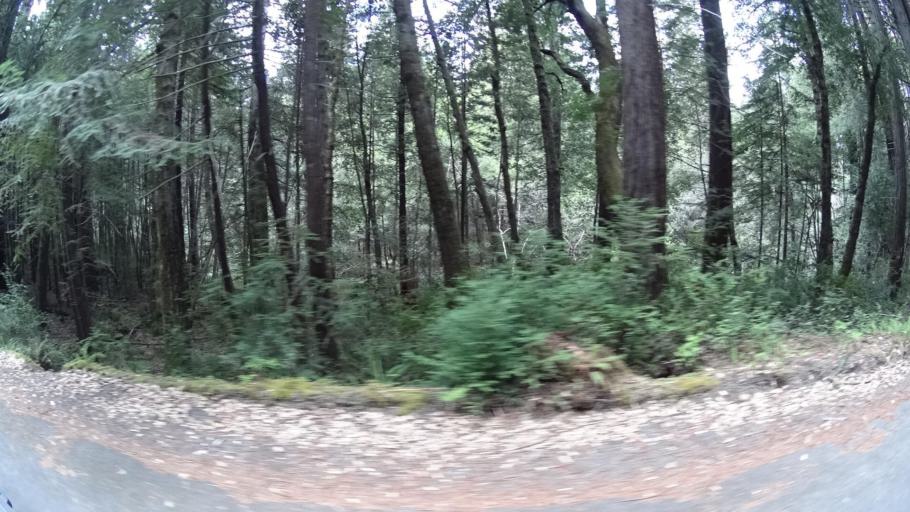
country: US
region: California
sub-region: Humboldt County
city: Redway
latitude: 39.9993
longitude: -123.9278
